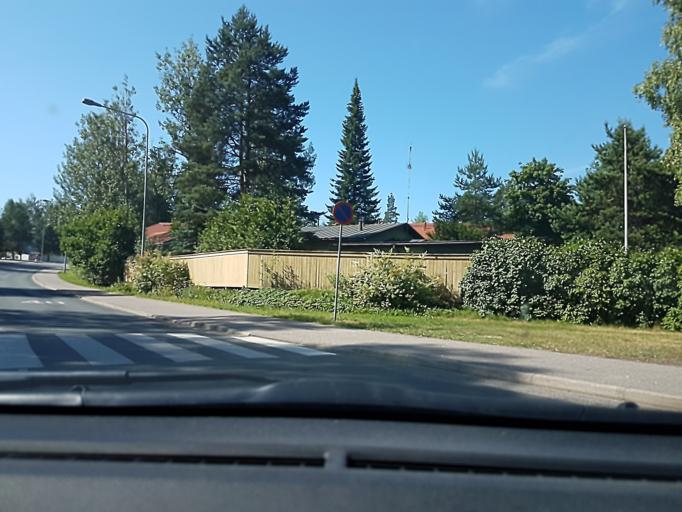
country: FI
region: Uusimaa
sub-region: Helsinki
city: Vantaa
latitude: 60.3132
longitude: 25.0325
